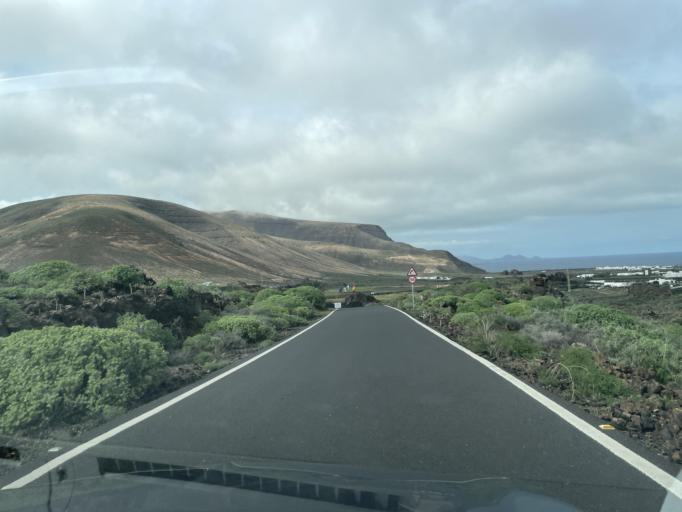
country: ES
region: Canary Islands
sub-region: Provincia de Las Palmas
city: Haria
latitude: 29.1996
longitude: -13.4517
